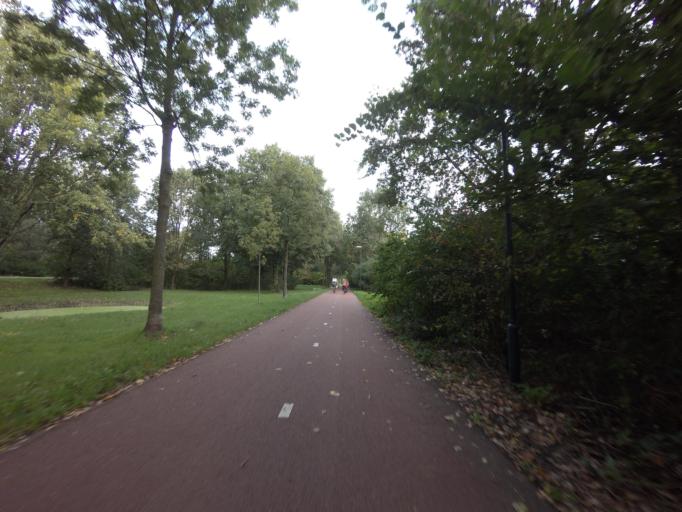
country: NL
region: North Brabant
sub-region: Gemeente Breda
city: Breda
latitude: 51.6057
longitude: 4.7486
